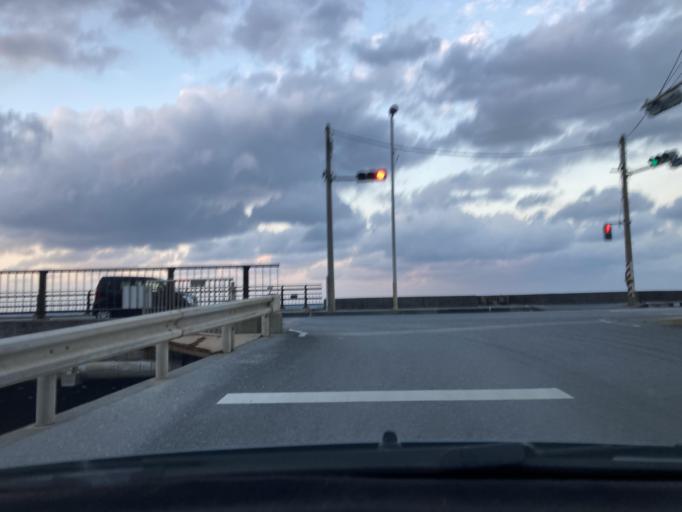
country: JP
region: Okinawa
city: Nago
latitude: 26.7030
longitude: 128.1201
